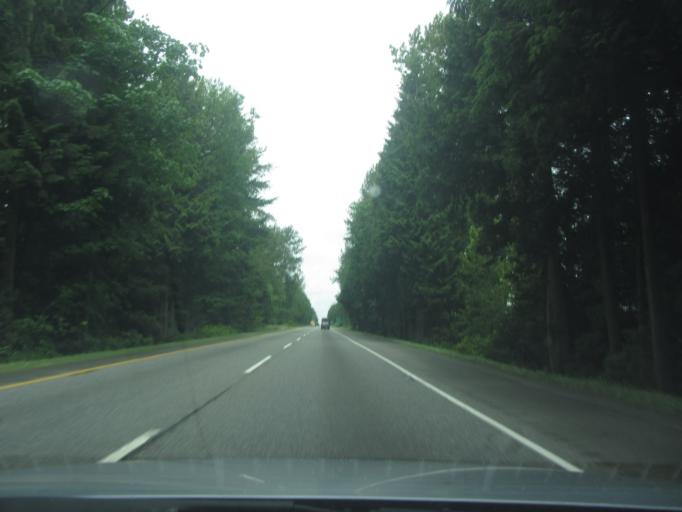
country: CA
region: British Columbia
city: Aldergrove
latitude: 49.0959
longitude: -122.4779
